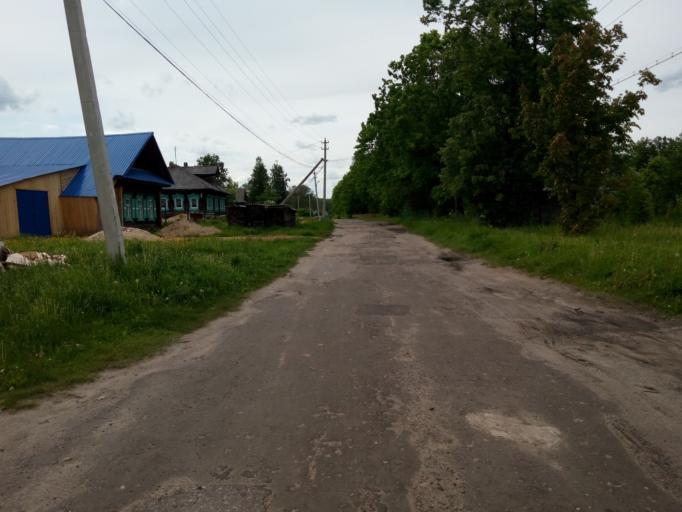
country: RU
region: Nizjnij Novgorod
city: Voskresenskoye
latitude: 56.7780
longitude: 45.5391
